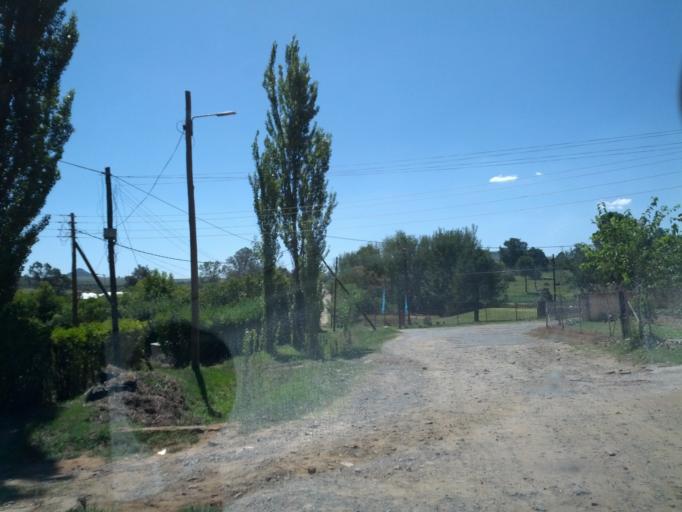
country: LS
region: Maseru
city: Maseru
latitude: -29.3132
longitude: 27.4701
